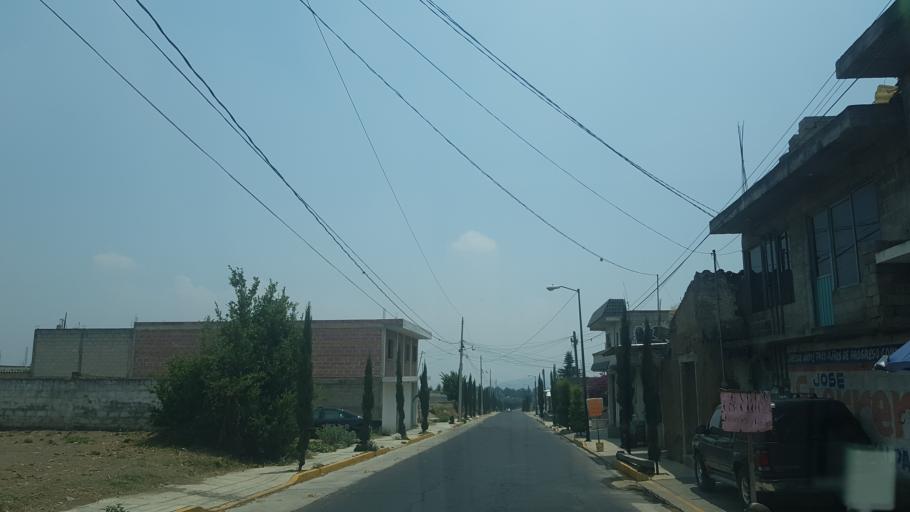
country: MX
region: Puebla
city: San Andres Calpan
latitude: 19.1038
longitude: -98.4500
